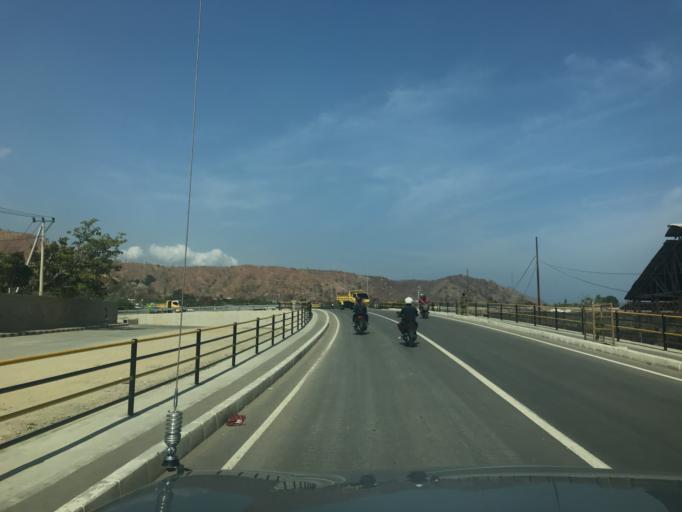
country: TL
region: Dili
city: Dili
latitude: -8.5609
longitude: 125.5360
